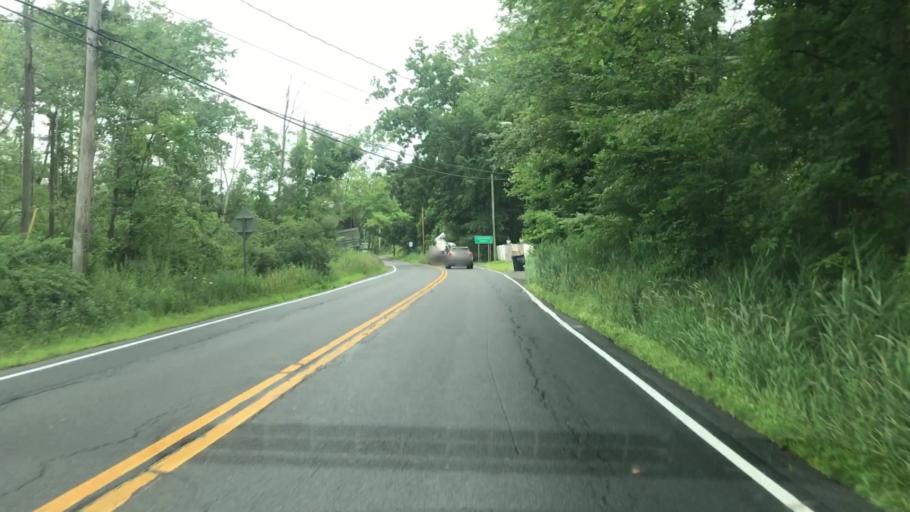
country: US
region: New York
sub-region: Westchester County
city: Jefferson Valley-Yorktown
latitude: 41.3426
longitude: -73.7876
